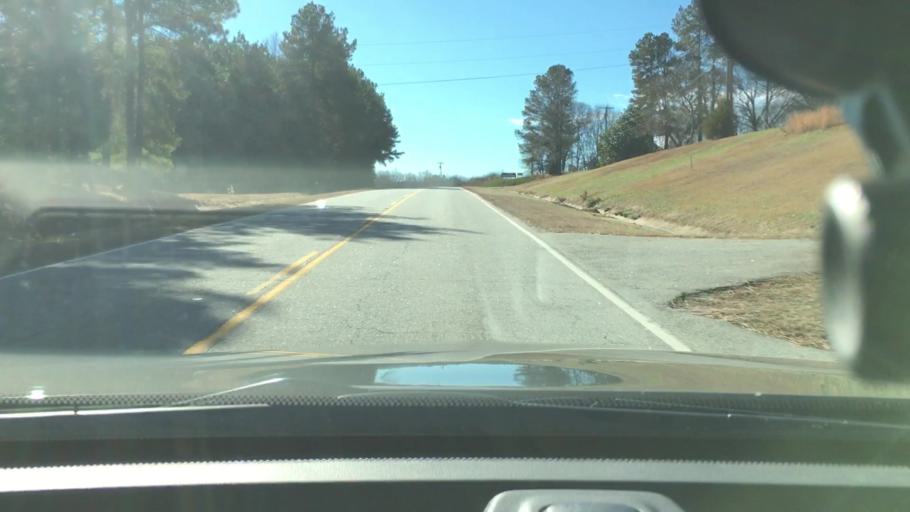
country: US
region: South Carolina
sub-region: Spartanburg County
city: Pacolet
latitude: 34.9712
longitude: -81.7040
